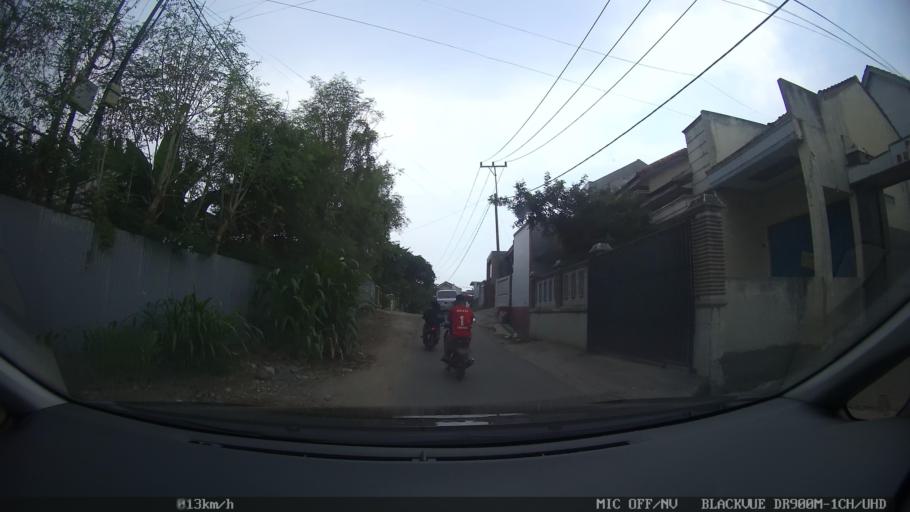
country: ID
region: Lampung
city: Kedaton
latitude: -5.3468
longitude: 105.2359
